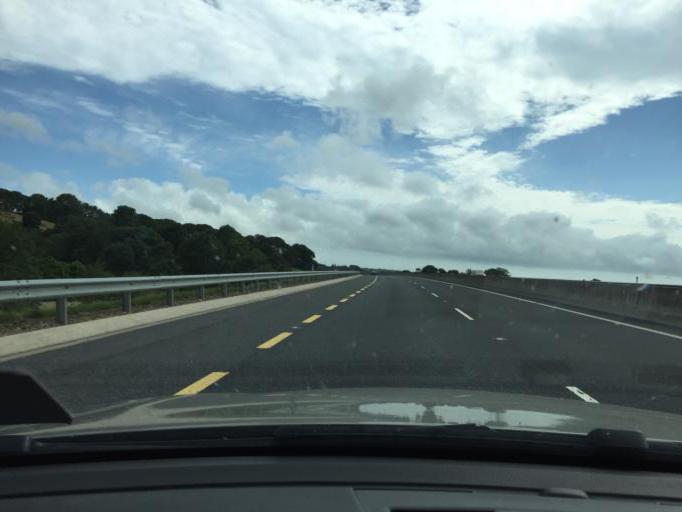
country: IE
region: Leinster
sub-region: Kilkenny
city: Mooncoin
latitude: 52.2519
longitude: -7.1907
